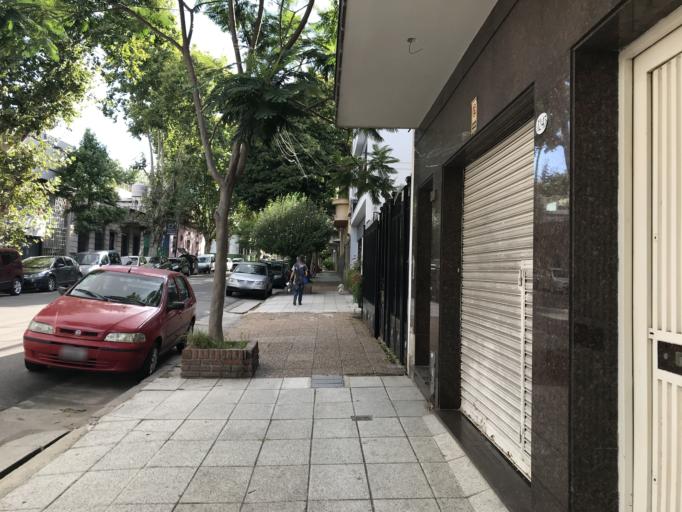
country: AR
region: Buenos Aires F.D.
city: Villa Santa Rita
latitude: -34.6307
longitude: -58.4447
